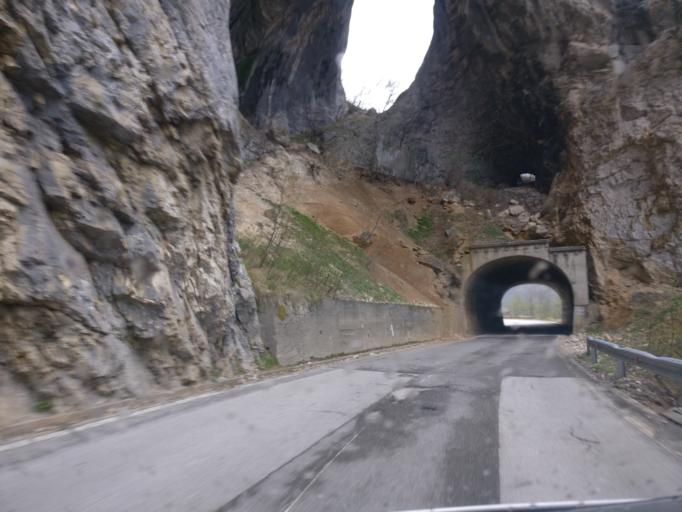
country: ME
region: Opstina Pluzine
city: Pluzine
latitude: 43.2313
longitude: 18.8458
